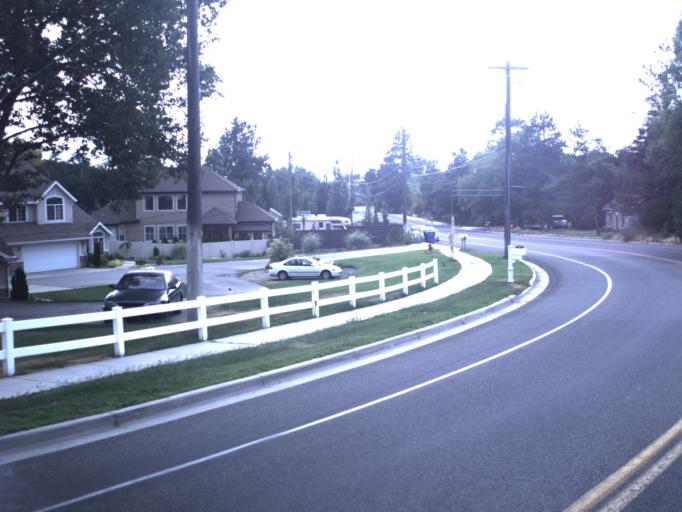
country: US
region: Utah
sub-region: Davis County
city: Farmington
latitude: 40.9902
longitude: -111.8880
